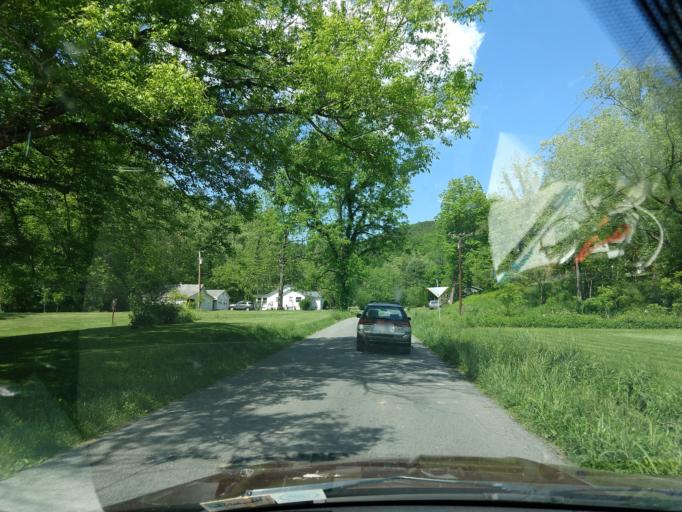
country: US
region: Virginia
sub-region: City of Covington
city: Fairlawn
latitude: 37.6927
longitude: -79.8891
